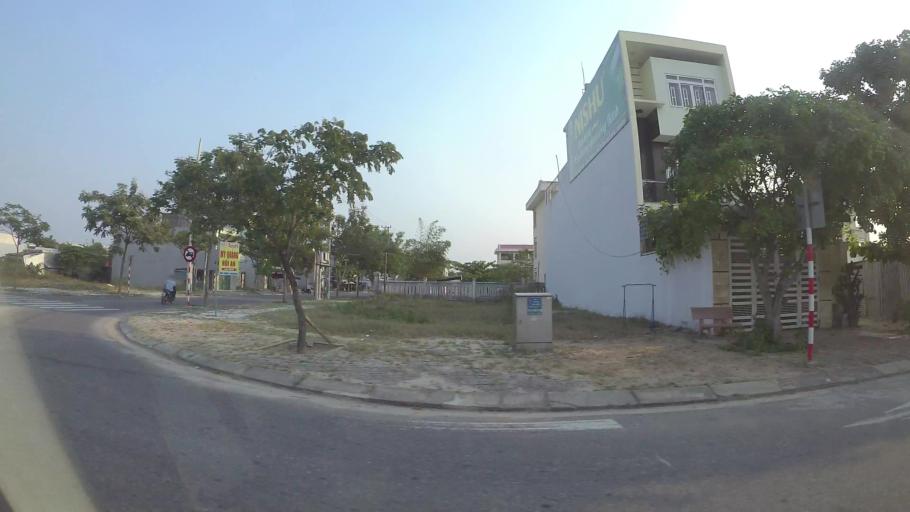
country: VN
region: Da Nang
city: Ngu Hanh Son
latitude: 15.9831
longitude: 108.2500
